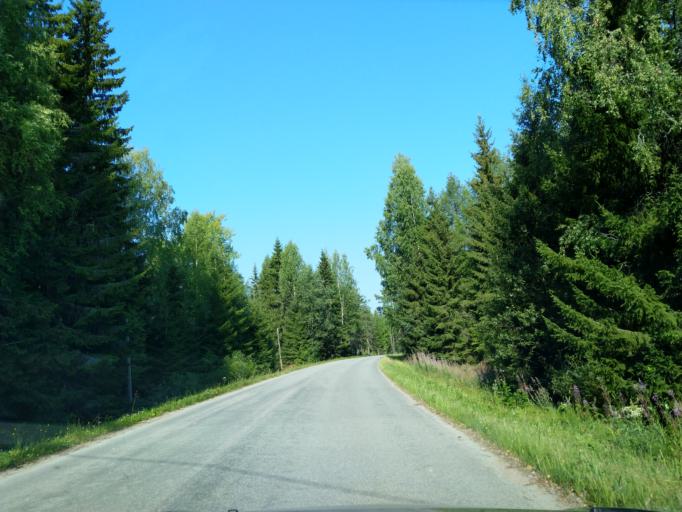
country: FI
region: Satakunta
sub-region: Pori
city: Laengelmaeki
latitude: 61.7257
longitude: 22.2050
